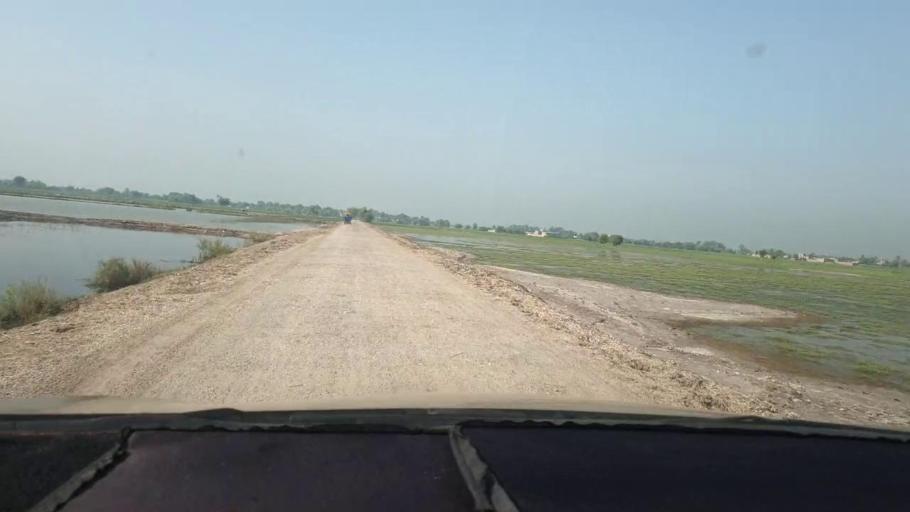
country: PK
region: Sindh
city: Kambar
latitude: 27.5769
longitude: 68.0889
